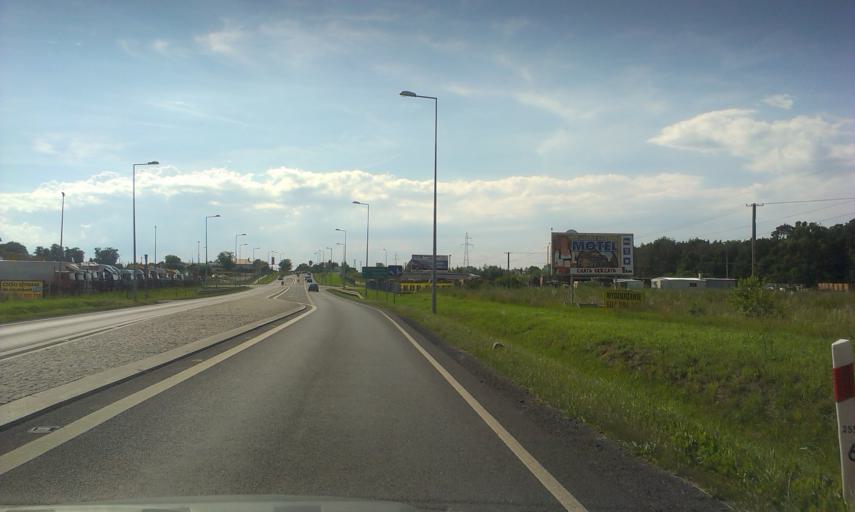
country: PL
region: Kujawsko-Pomorskie
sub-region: Powiat bydgoski
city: Sicienko
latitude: 53.1579
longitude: 17.8521
